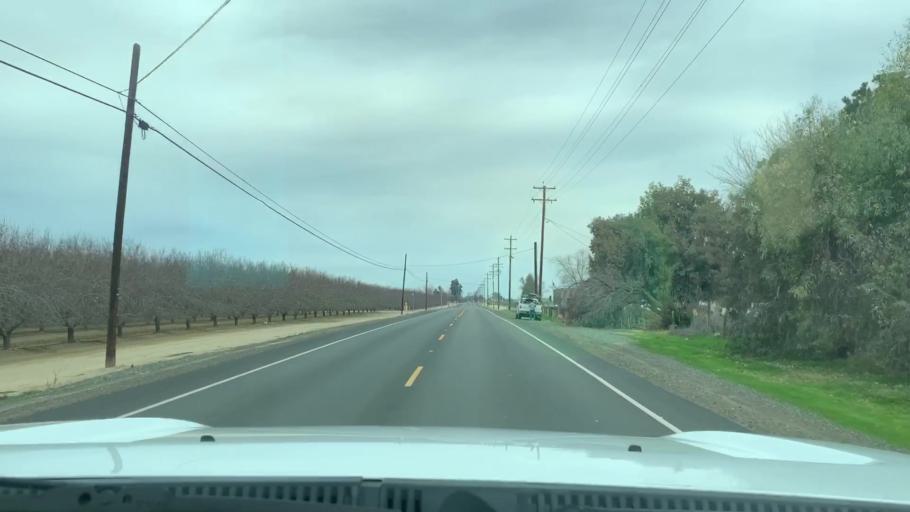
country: US
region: California
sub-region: Kern County
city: Shafter
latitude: 35.4258
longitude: -119.2519
